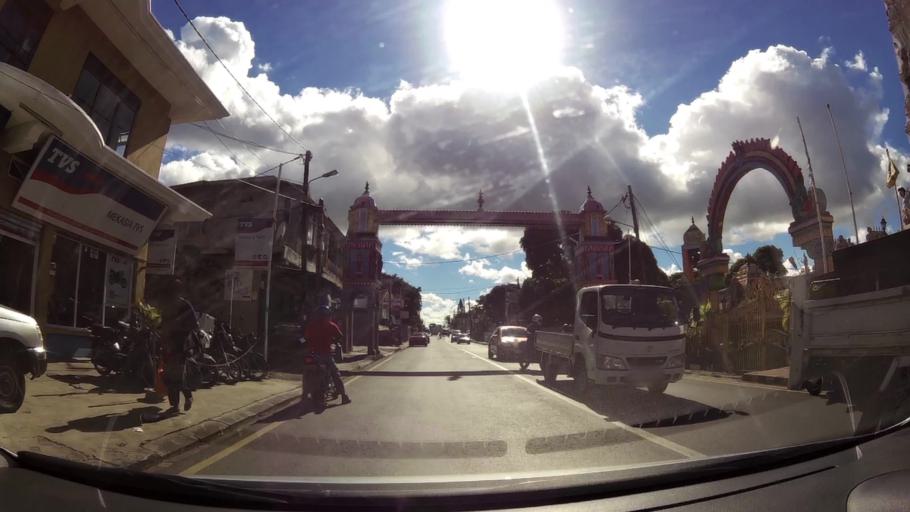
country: MU
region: Pamplemousses
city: Le Hochet
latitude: -20.1342
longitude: 57.5279
